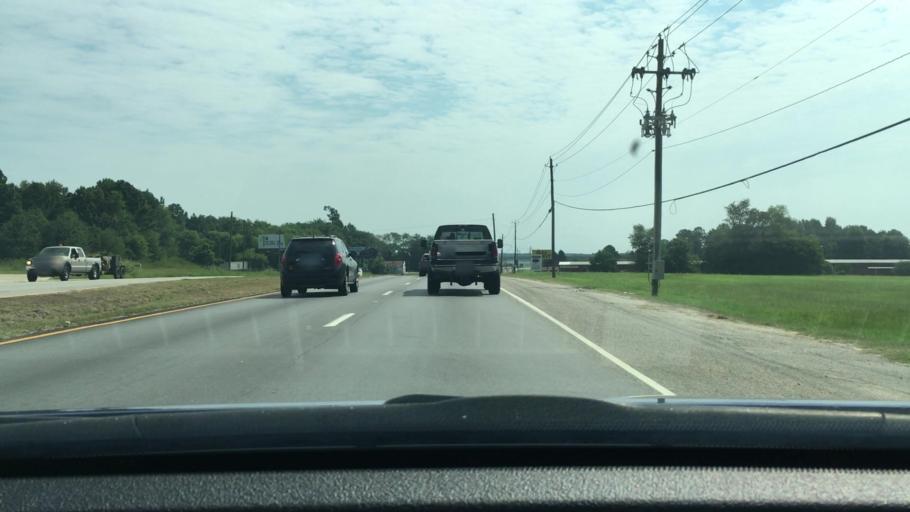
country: US
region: South Carolina
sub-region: Sumter County
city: Oakland
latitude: 33.9517
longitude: -80.4966
